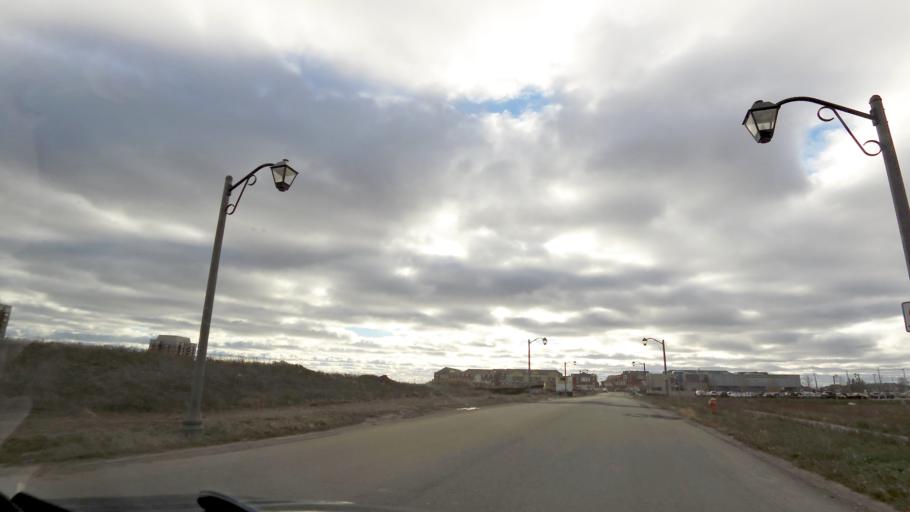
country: CA
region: Ontario
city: Oakville
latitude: 43.4824
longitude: -79.7231
